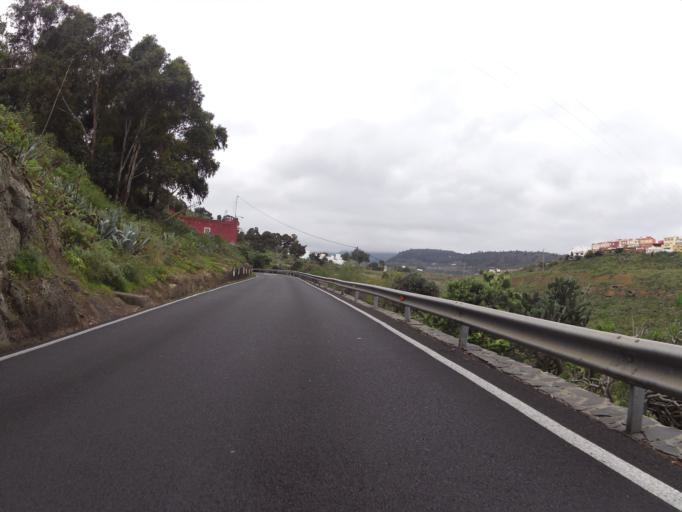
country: ES
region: Canary Islands
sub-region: Provincia de Las Palmas
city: Arucas
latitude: 28.0945
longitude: -15.4989
